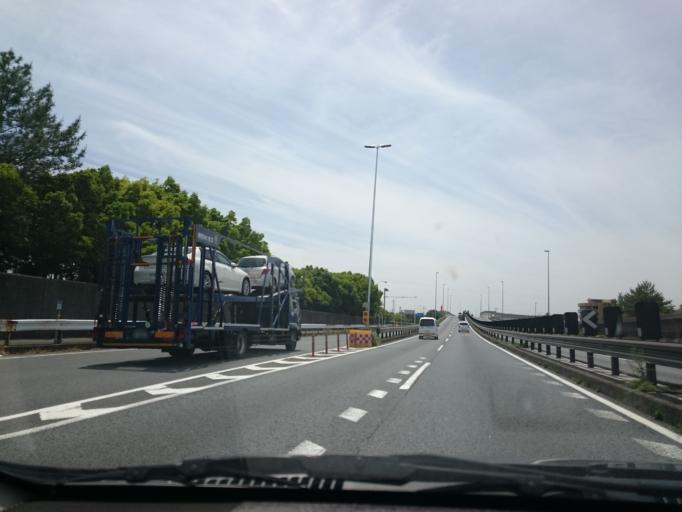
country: JP
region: Mie
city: Yokkaichi
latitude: 34.9956
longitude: 136.6524
